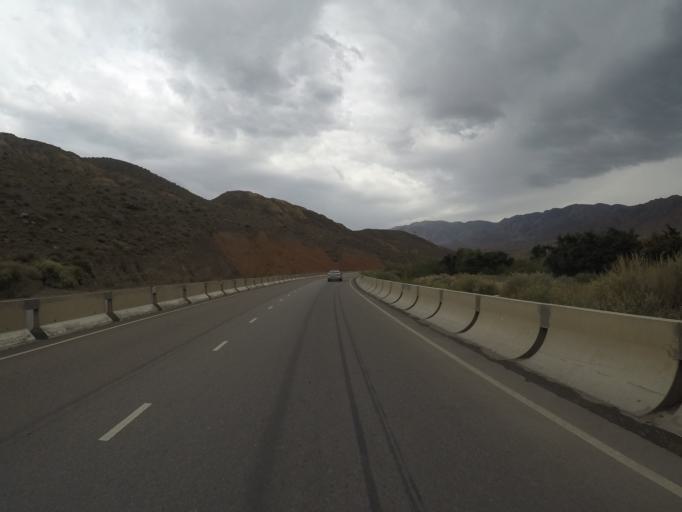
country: KG
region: Naryn
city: Kochkor
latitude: 42.4848
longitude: 75.8651
